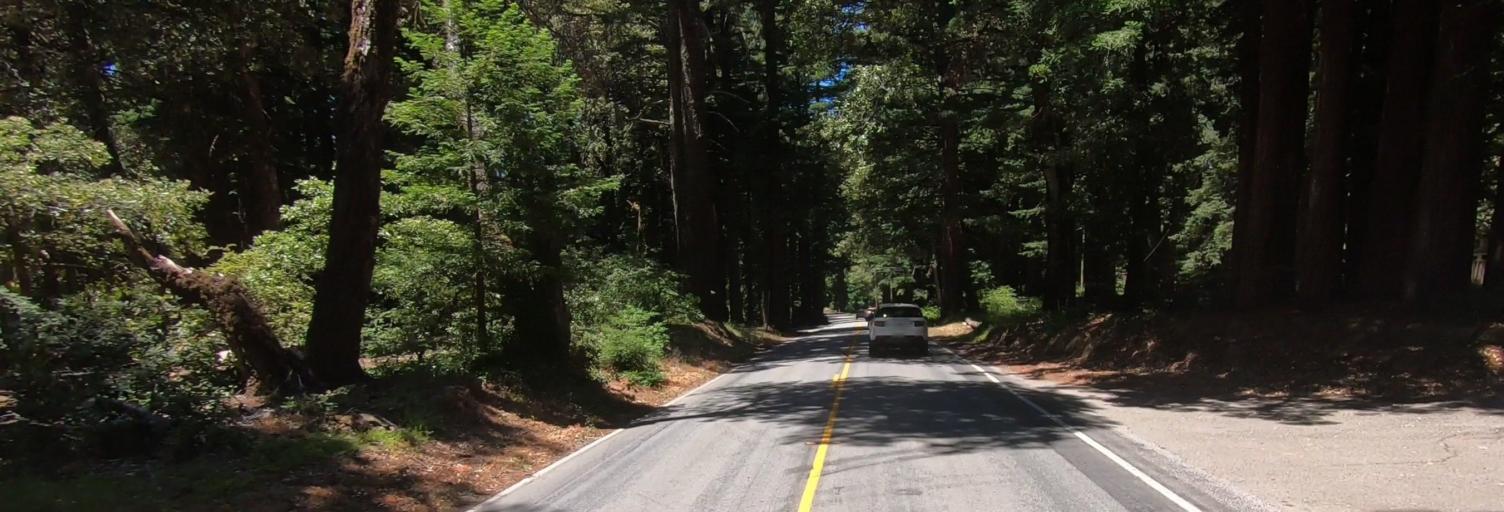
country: US
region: California
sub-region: San Mateo County
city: Emerald Lake Hills
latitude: 37.4434
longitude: -122.3298
